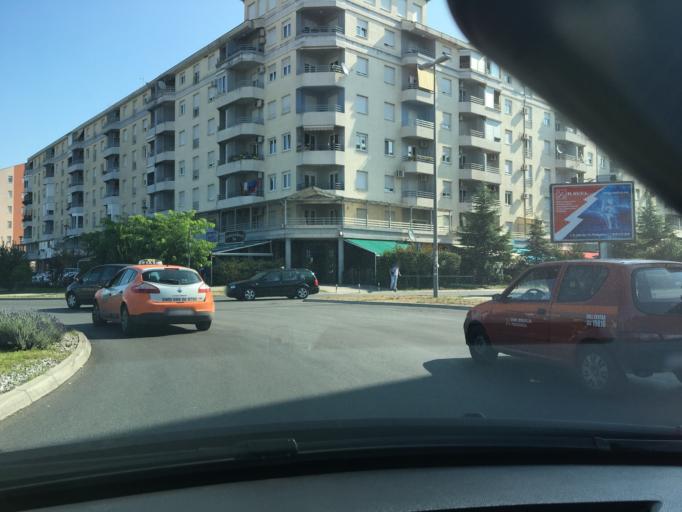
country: ME
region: Podgorica
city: Podgorica
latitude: 42.4354
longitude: 19.2751
